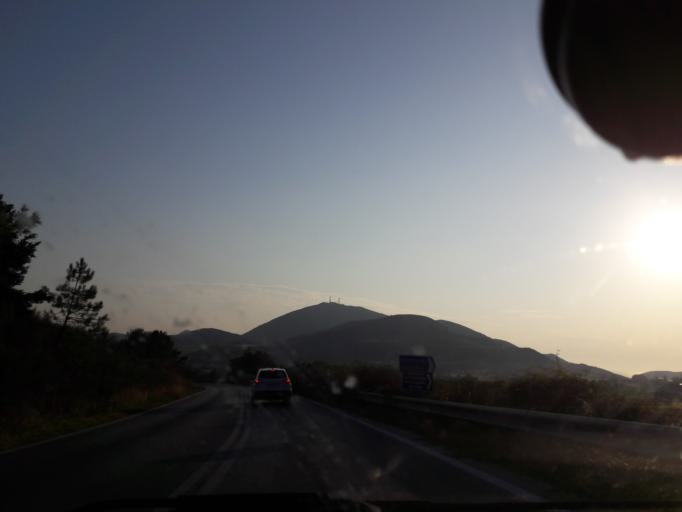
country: GR
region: North Aegean
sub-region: Nomos Lesvou
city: Myrina
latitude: 39.9124
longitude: 25.1139
